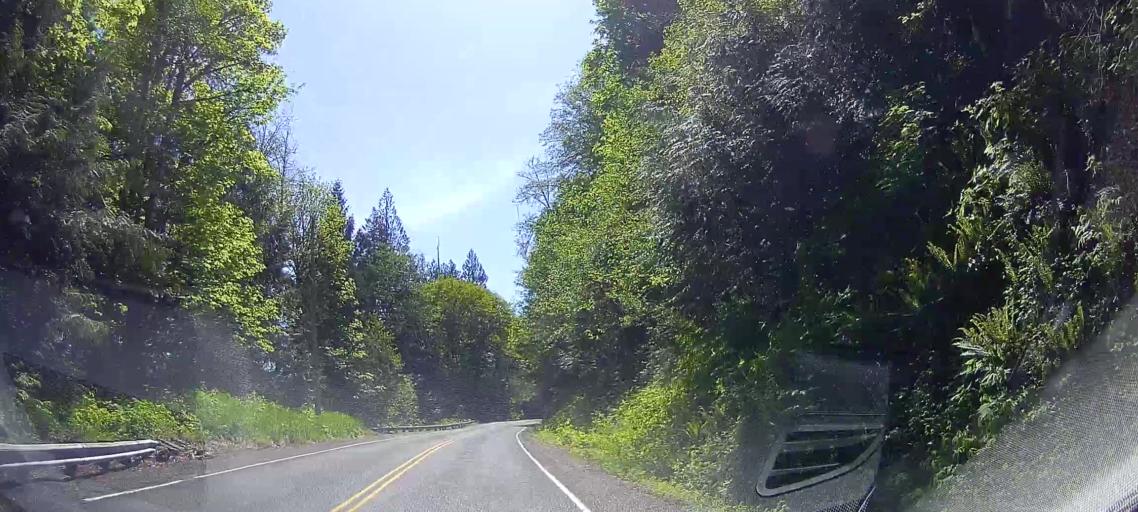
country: US
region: Washington
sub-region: Snohomish County
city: Darrington
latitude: 48.4796
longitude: -121.6501
